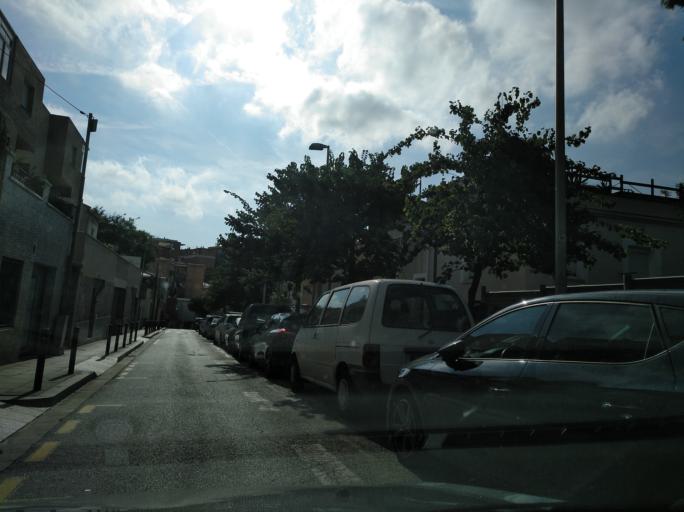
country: ES
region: Catalonia
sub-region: Provincia de Barcelona
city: Sarria-Sant Gervasi
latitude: 41.4218
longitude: 2.1447
